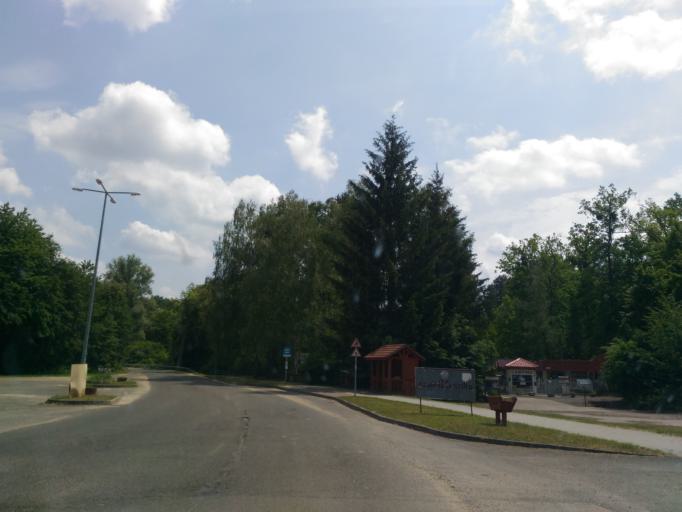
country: HU
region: Baranya
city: Komlo
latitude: 46.1755
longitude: 18.2226
